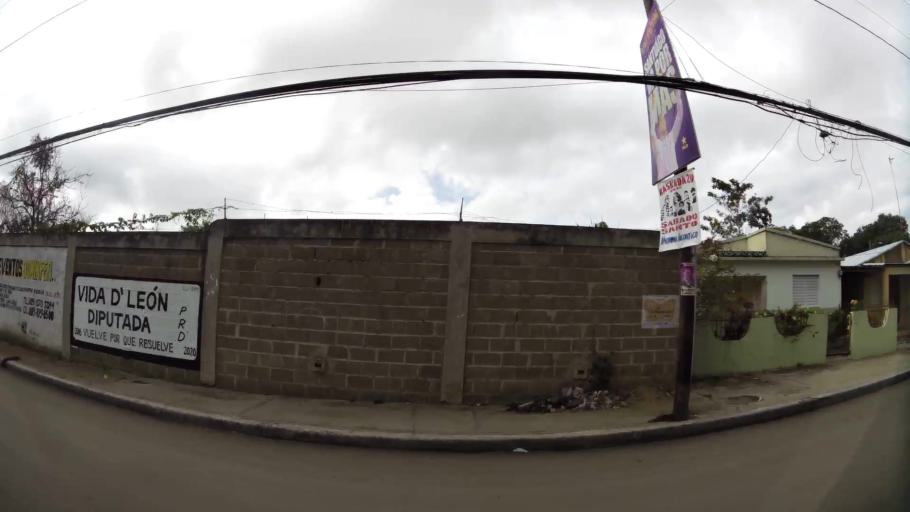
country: DO
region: Santiago
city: Santiago de los Caballeros
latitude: 19.4258
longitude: -70.6539
